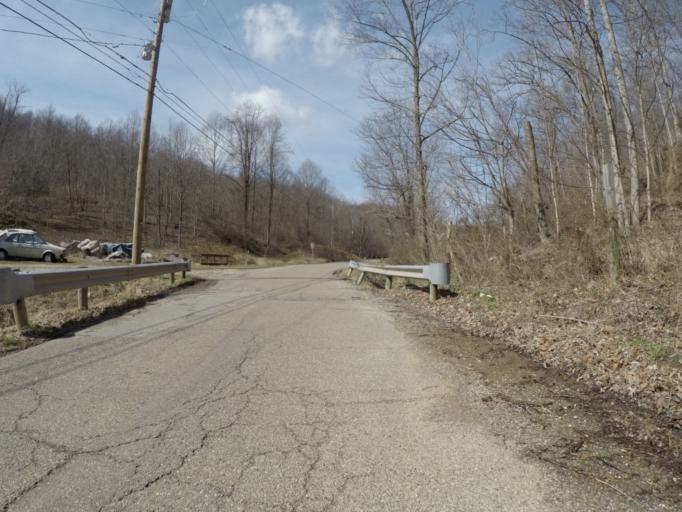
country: US
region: Ohio
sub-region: Lawrence County
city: Burlington
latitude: 38.4804
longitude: -82.5282
